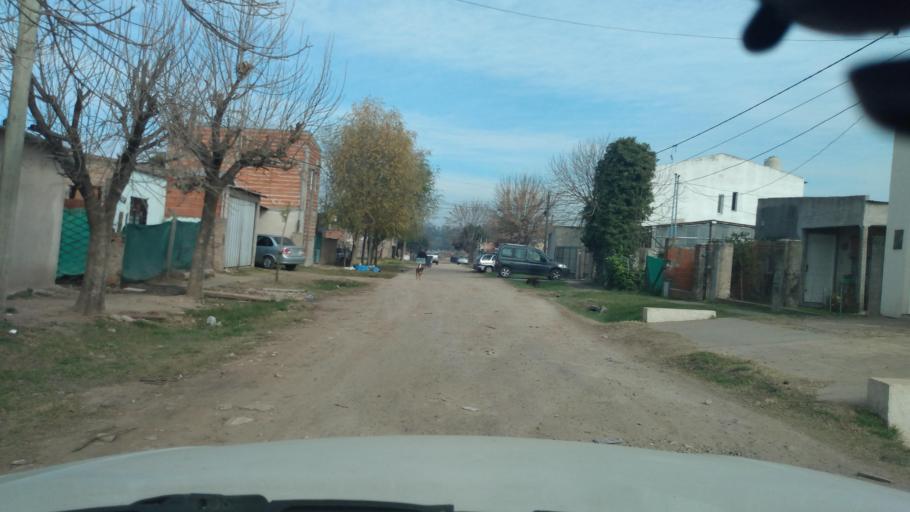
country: AR
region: Buenos Aires
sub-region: Partido de Lujan
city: Lujan
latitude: -34.5803
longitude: -59.1246
